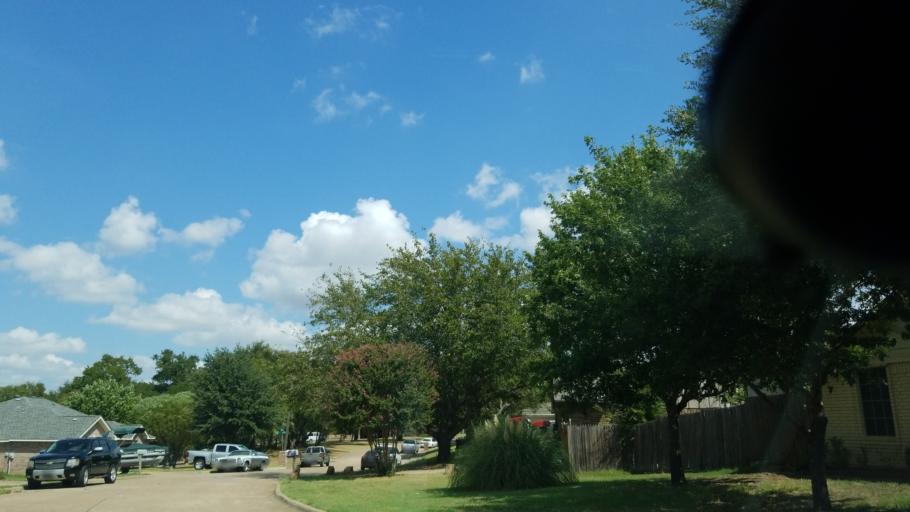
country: US
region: Texas
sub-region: Dallas County
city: Grand Prairie
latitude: 32.7173
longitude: -96.9920
